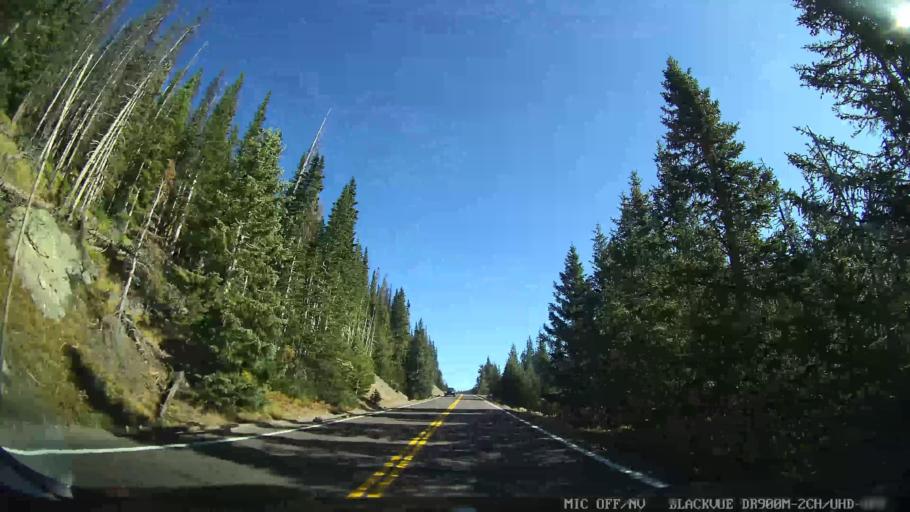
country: US
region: Colorado
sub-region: Larimer County
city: Estes Park
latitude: 40.4184
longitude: -105.8149
